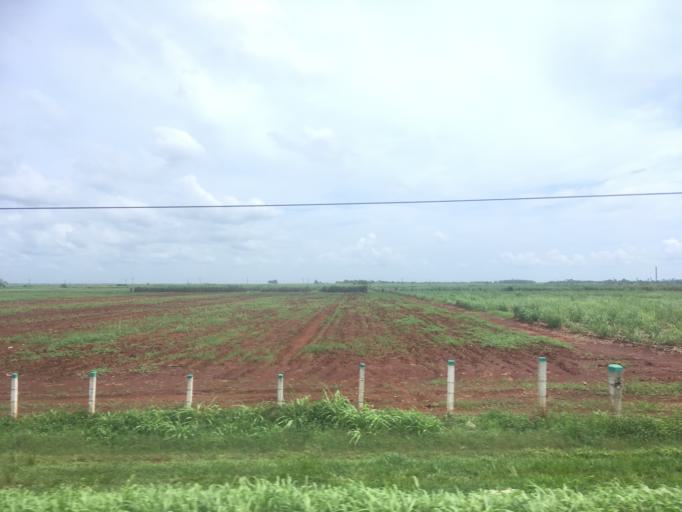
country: CU
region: Matanzas
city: Jovellanos
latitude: 22.7972
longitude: -81.1498
